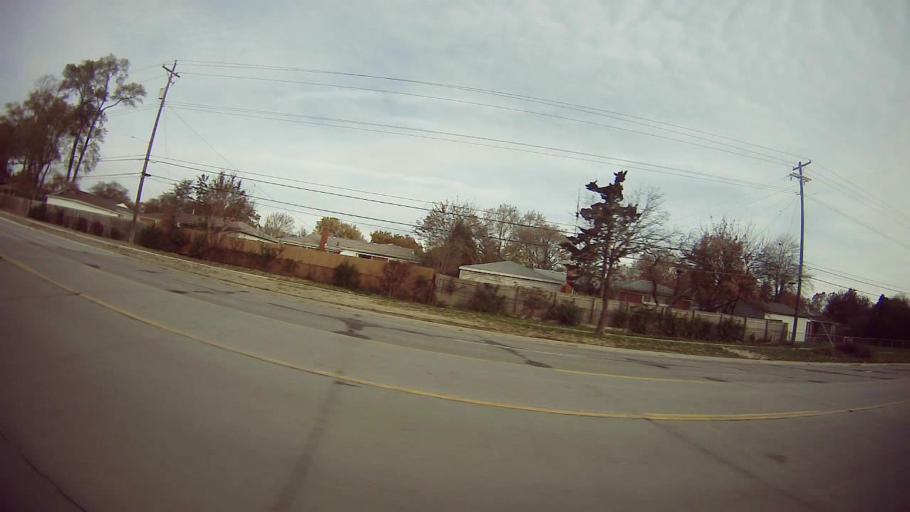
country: US
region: Michigan
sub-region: Oakland County
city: Southfield
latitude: 42.4736
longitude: -83.2080
